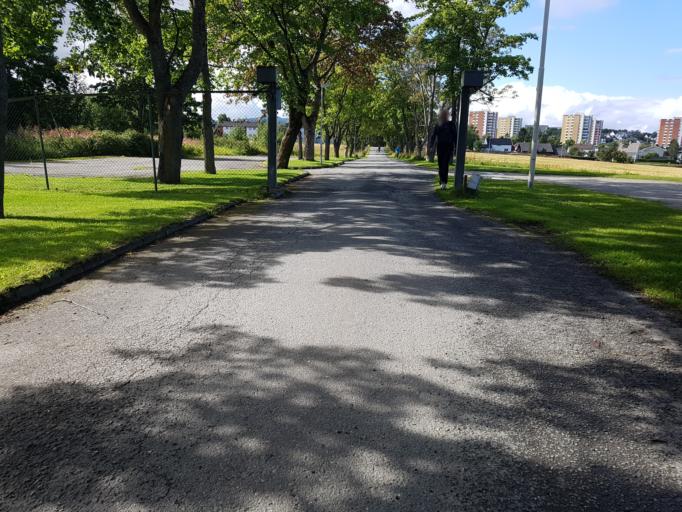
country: NO
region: Sor-Trondelag
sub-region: Trondheim
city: Trondheim
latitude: 63.4197
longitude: 10.4536
